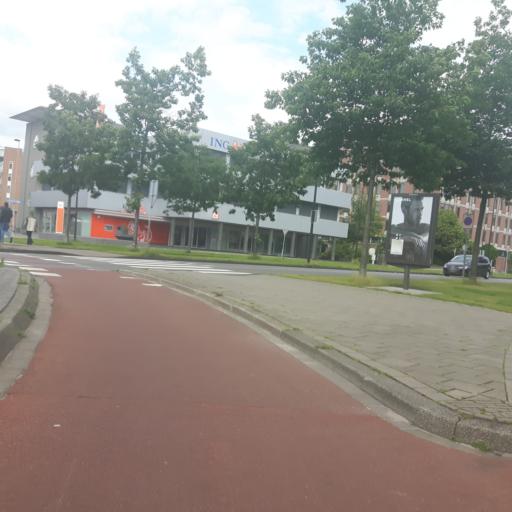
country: NL
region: Overijssel
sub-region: Gemeente Enschede
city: Enschede
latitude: 52.2180
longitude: 6.8912
